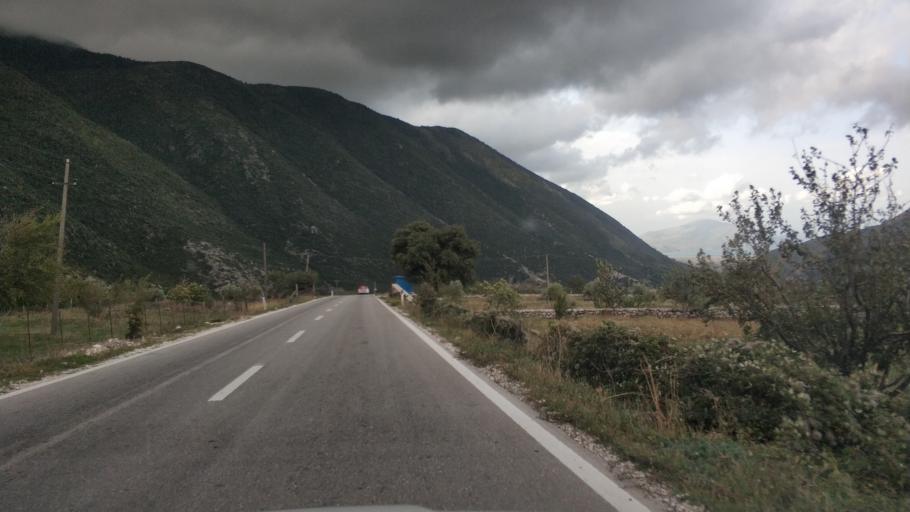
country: AL
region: Vlore
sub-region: Rrethi i Vlores
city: Brataj
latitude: 40.2311
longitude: 19.5680
